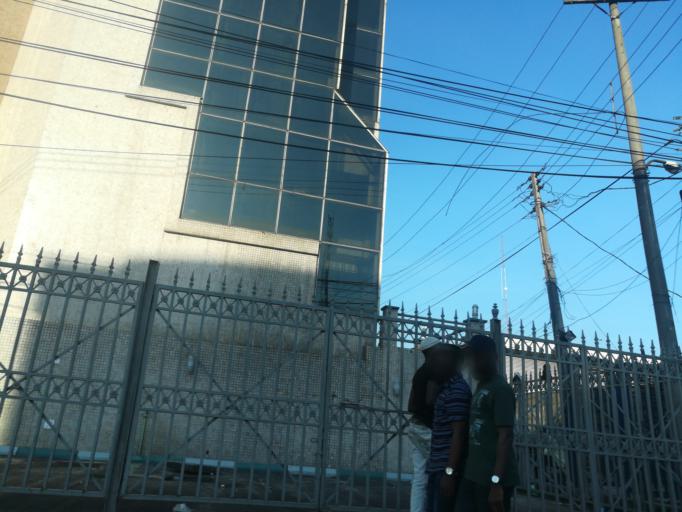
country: NG
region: Lagos
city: Ikeja
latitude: 6.6033
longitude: 3.3513
